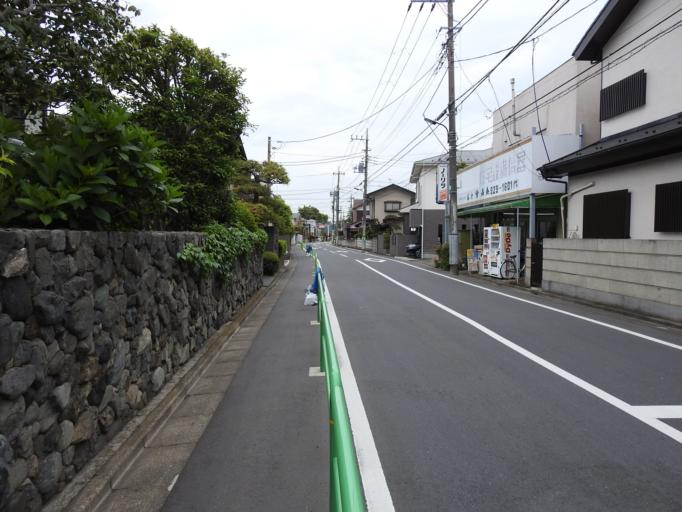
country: JP
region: Tokyo
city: Musashino
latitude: 35.7341
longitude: 139.5852
